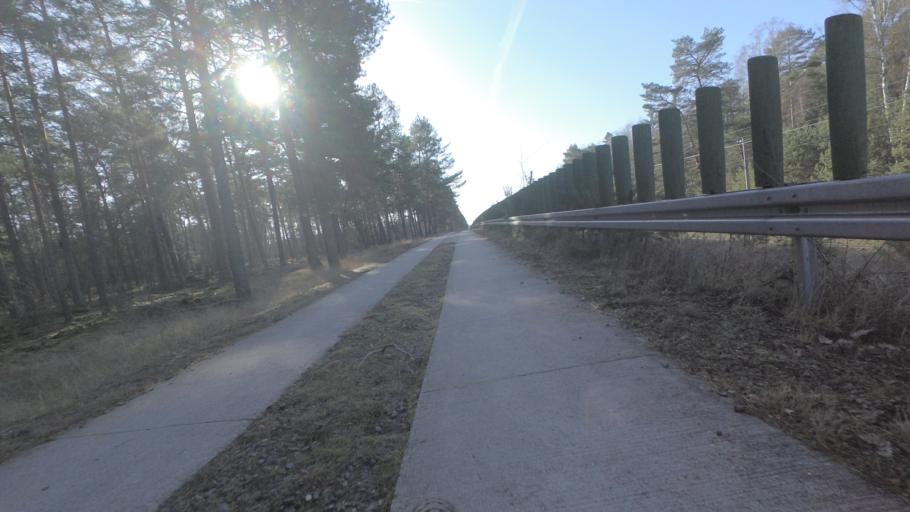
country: DE
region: Brandenburg
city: Trebbin
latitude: 52.1547
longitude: 13.2203
